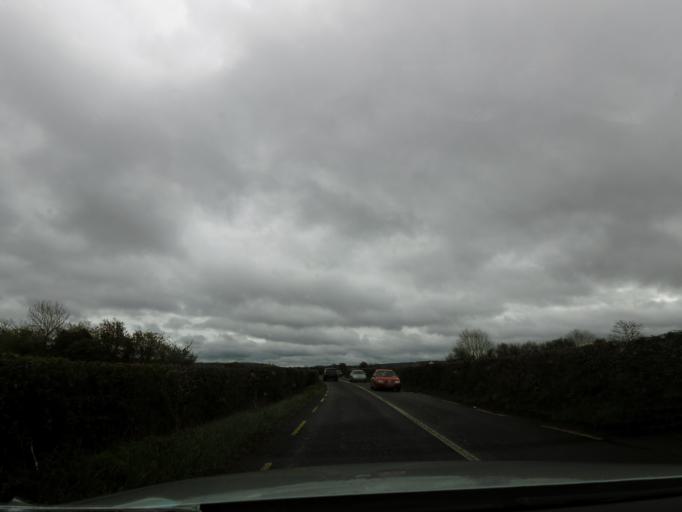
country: IE
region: Leinster
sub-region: Laois
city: Rathdowney
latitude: 52.7219
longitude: -7.5387
